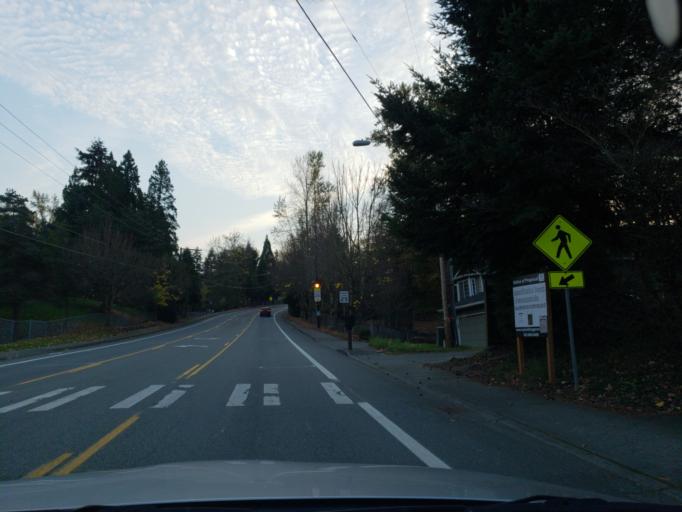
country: US
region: Washington
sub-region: King County
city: Woodinville
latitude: 47.7507
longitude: -122.1797
